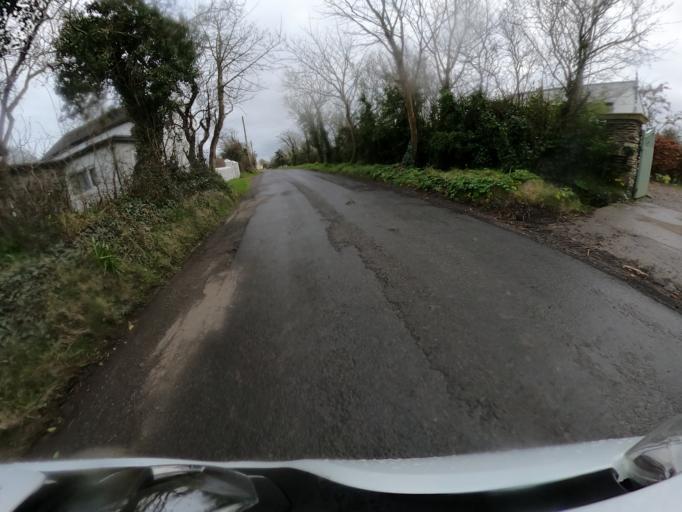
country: IM
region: Ramsey
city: Ramsey
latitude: 54.3770
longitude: -4.4471
